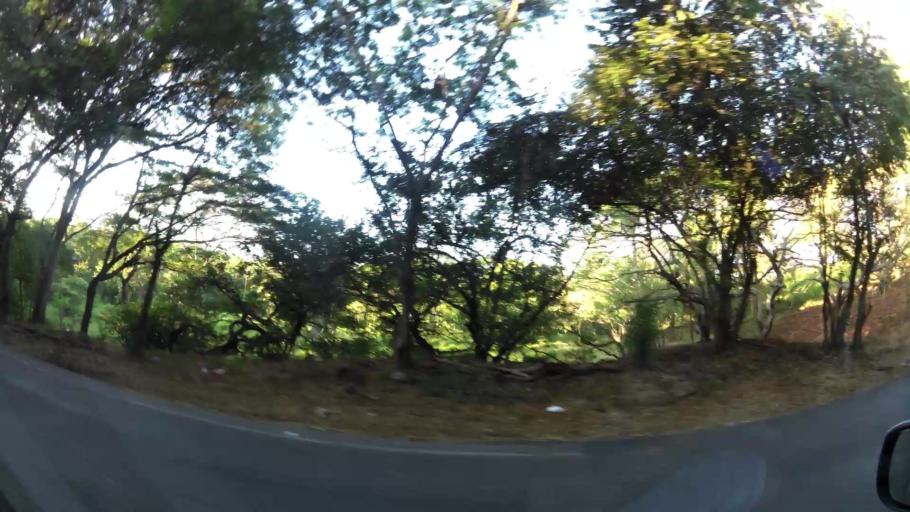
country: CR
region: Puntarenas
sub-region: Canton Central de Puntarenas
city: Chacarita
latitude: 10.0237
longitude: -84.7352
